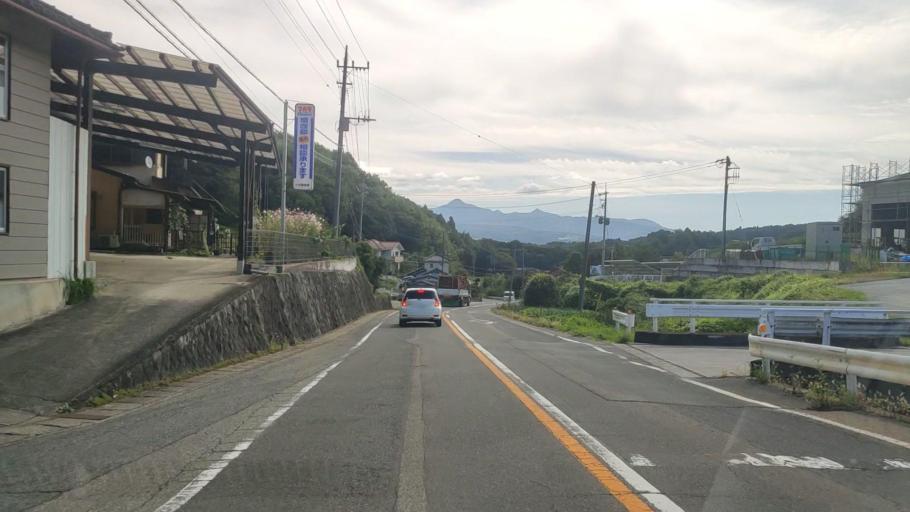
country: JP
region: Gunma
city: Numata
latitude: 36.6263
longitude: 139.0196
